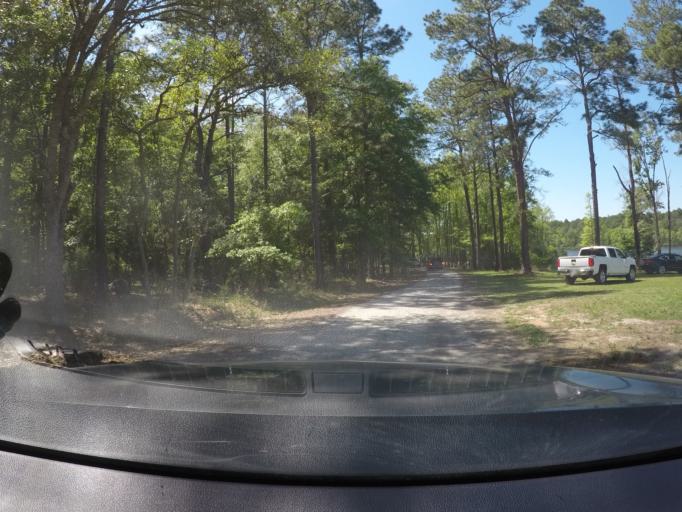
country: US
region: Georgia
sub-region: Evans County
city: Claxton
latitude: 32.1280
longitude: -81.7947
